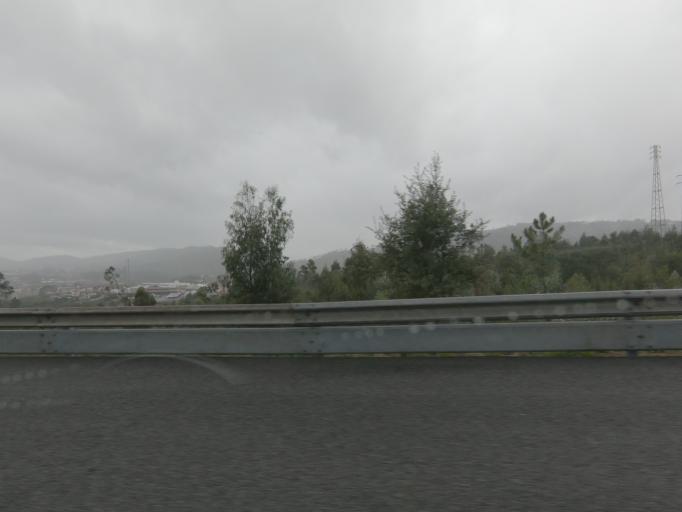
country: PT
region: Porto
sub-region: Valongo
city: Campo
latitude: 41.1885
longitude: -8.4775
